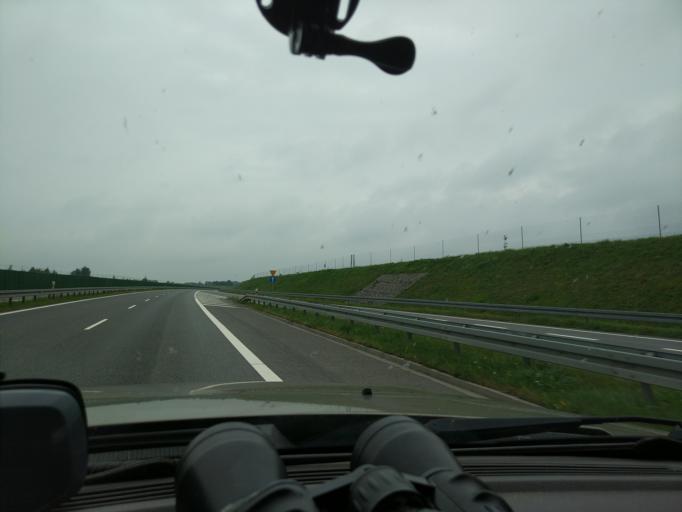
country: PL
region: Podlasie
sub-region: Powiat zambrowski
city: Zambrow
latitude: 52.9839
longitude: 22.2152
